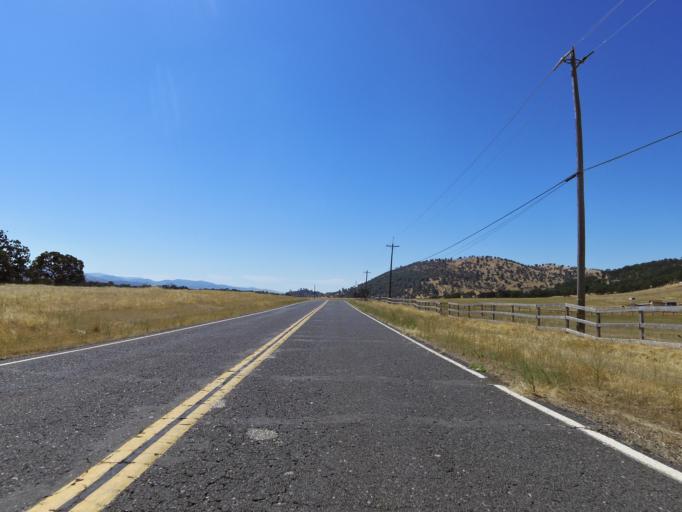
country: US
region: California
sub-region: Tuolumne County
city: Tuolumne City
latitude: 37.6428
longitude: -120.3098
